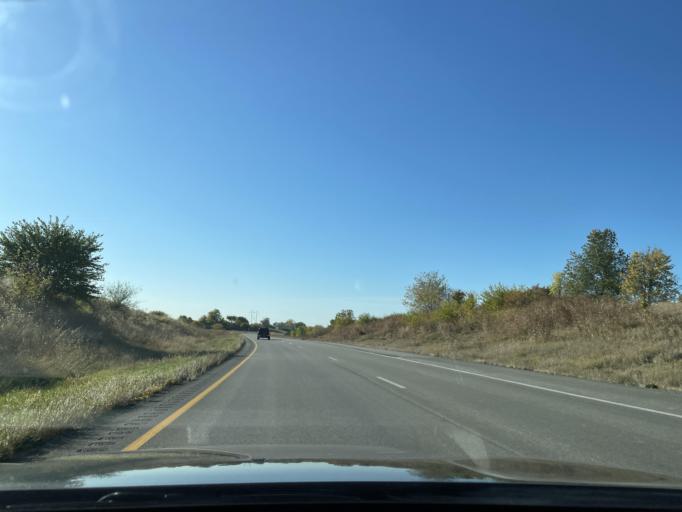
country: US
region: Missouri
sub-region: Andrew County
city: Country Club Village
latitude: 39.8838
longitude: -94.8583
